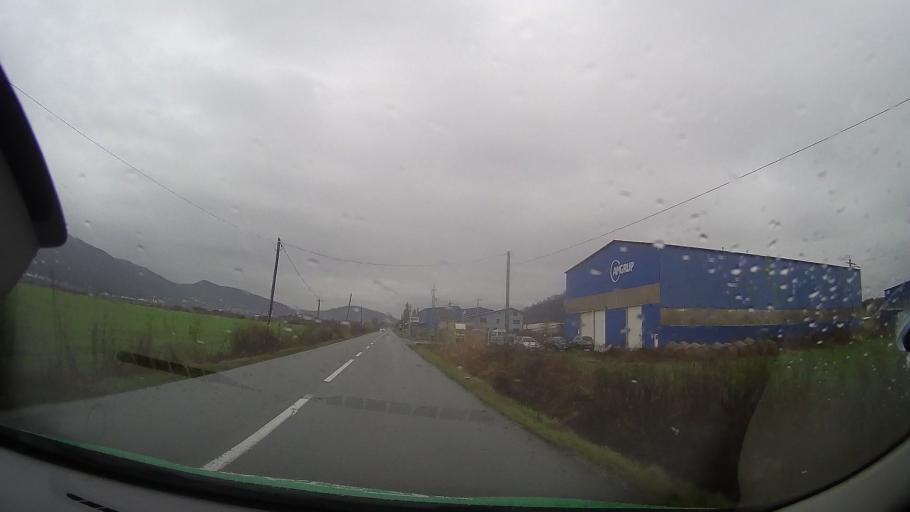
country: RO
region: Bistrita-Nasaud
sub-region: Municipiul Bistrita
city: Viisoara
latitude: 47.0591
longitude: 24.4357
